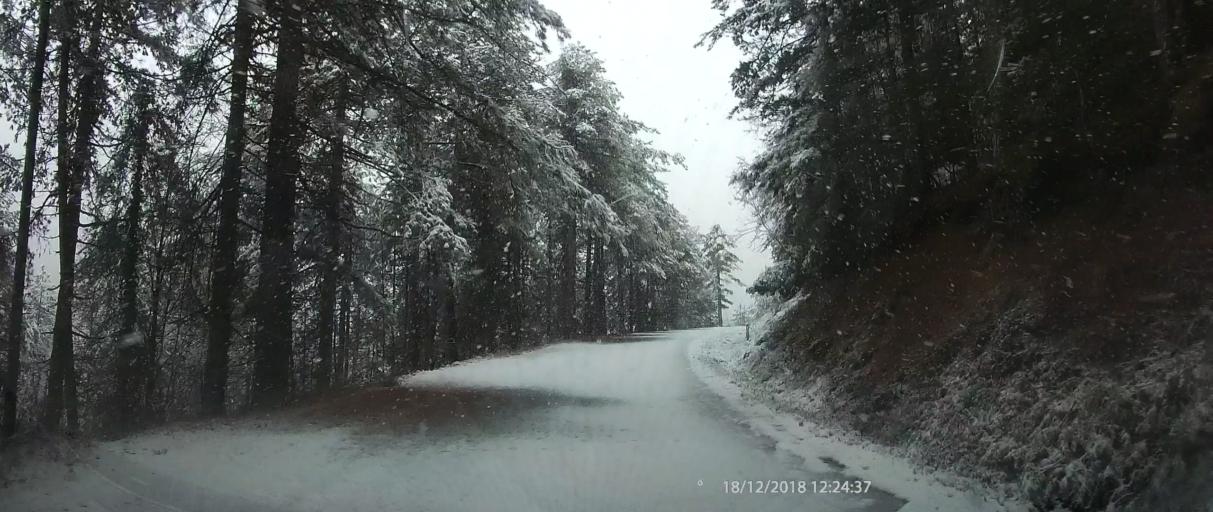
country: GR
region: Central Macedonia
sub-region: Nomos Pierias
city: Litochoro
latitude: 40.0913
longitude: 22.4160
